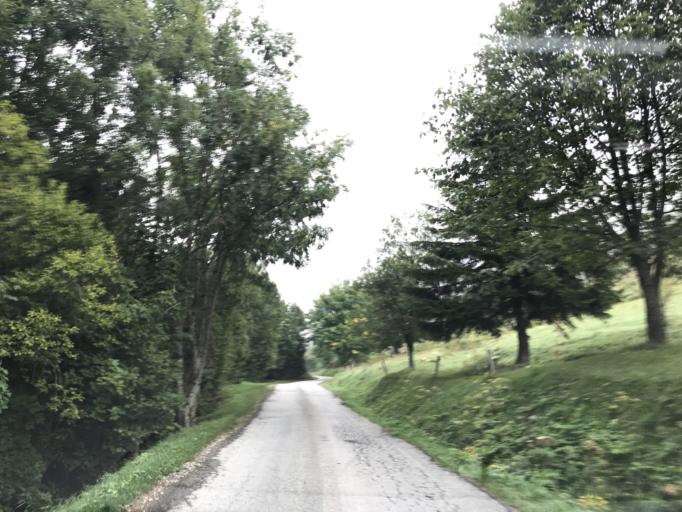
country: FR
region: Rhone-Alpes
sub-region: Departement de la Haute-Savoie
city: Talloires
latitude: 45.8215
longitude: 6.2619
